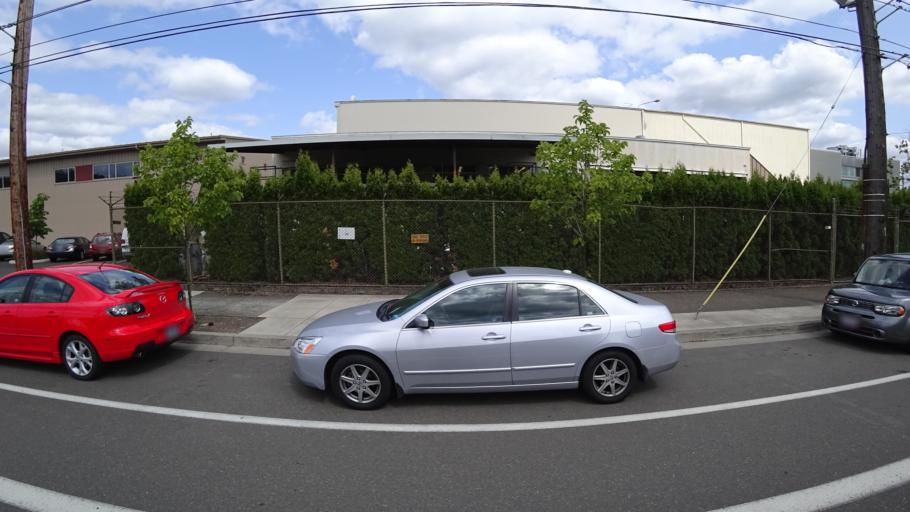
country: US
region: Oregon
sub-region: Multnomah County
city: Portland
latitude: 45.4944
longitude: -122.6483
